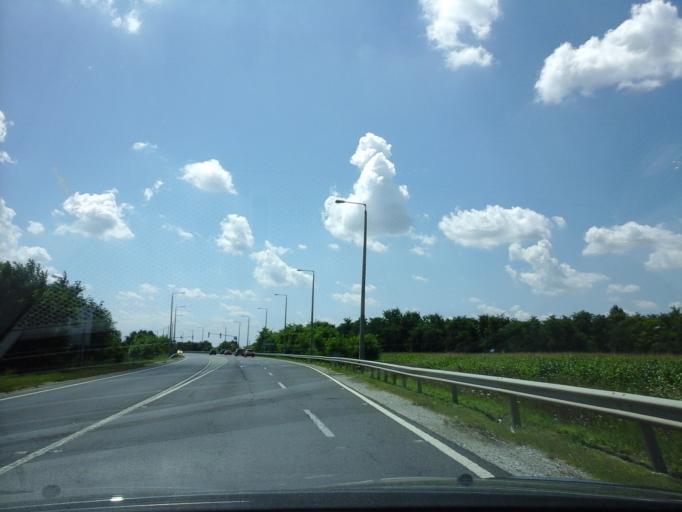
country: HU
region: Hajdu-Bihar
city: Hajduszoboszlo
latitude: 47.4614
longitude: 21.4487
